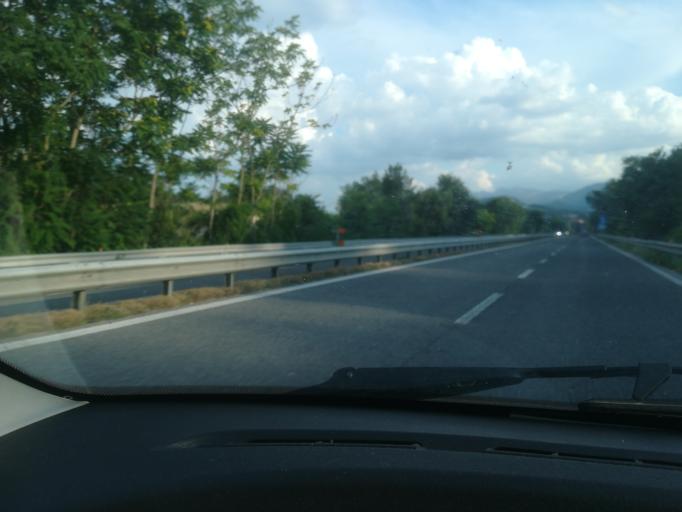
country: IT
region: The Marches
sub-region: Provincia di Macerata
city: Belforte del Chienti
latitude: 43.1752
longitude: 13.2489
